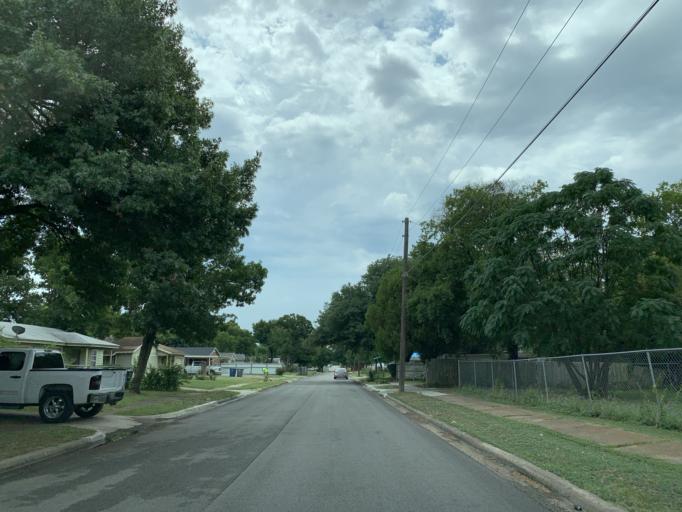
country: US
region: Texas
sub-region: Dallas County
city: DeSoto
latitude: 32.6599
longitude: -96.8319
